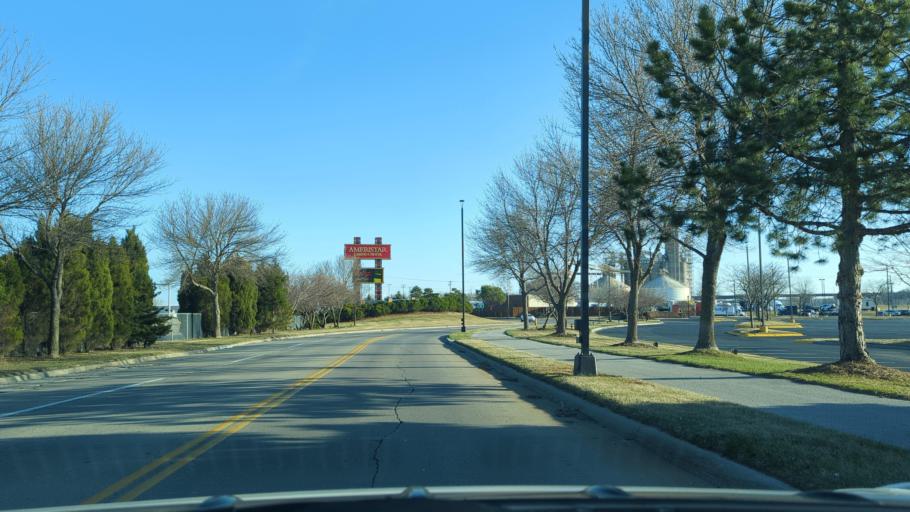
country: US
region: Nebraska
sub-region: Douglas County
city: Omaha
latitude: 41.2429
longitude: -95.9079
